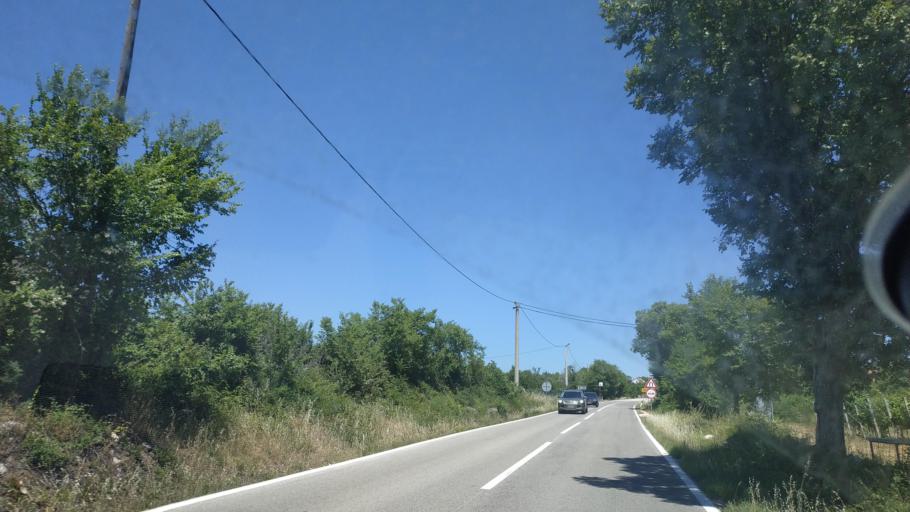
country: HR
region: Sibensko-Kniniska
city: Drnis
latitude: 43.8844
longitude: 16.2057
